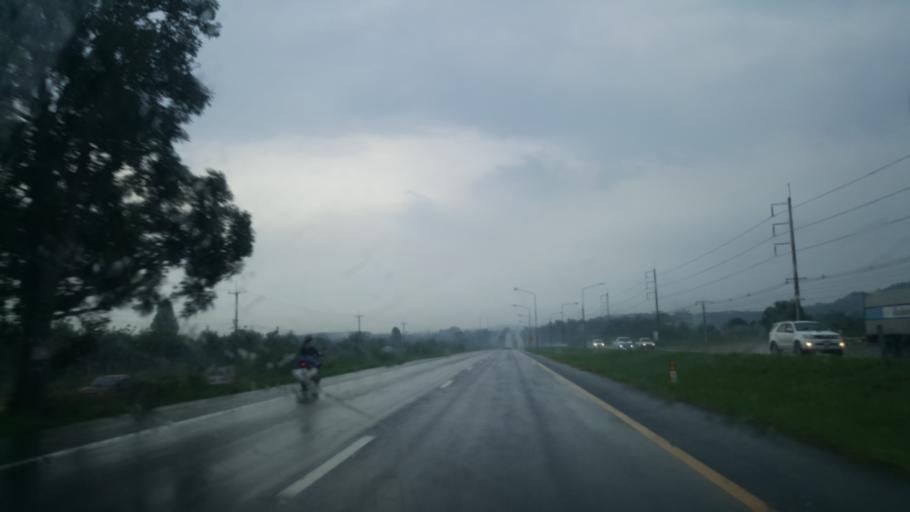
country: TH
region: Chon Buri
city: Ban Talat Bueng
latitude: 12.9765
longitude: 101.0578
